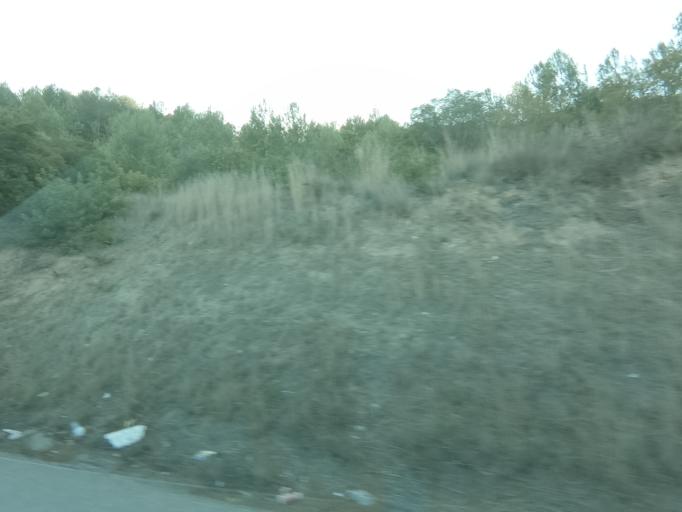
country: PT
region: Setubal
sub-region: Palmela
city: Quinta do Anjo
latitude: 38.5229
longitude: -8.9835
